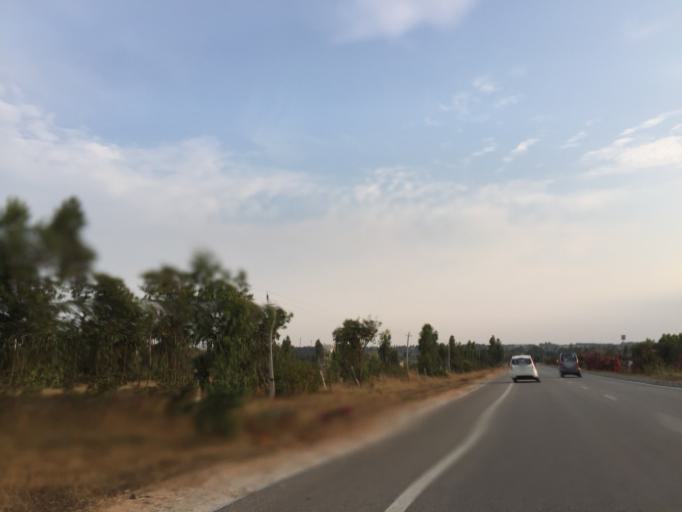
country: IN
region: Karnataka
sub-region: Chikkaballapur
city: Chik Ballapur
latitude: 13.4001
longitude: 77.7423
